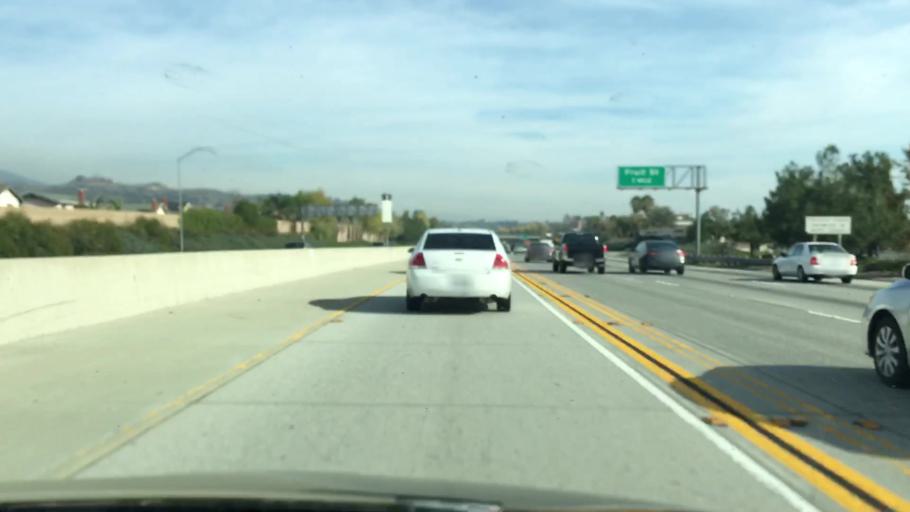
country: US
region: California
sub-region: Los Angeles County
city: La Verne
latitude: 34.1199
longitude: -117.7843
